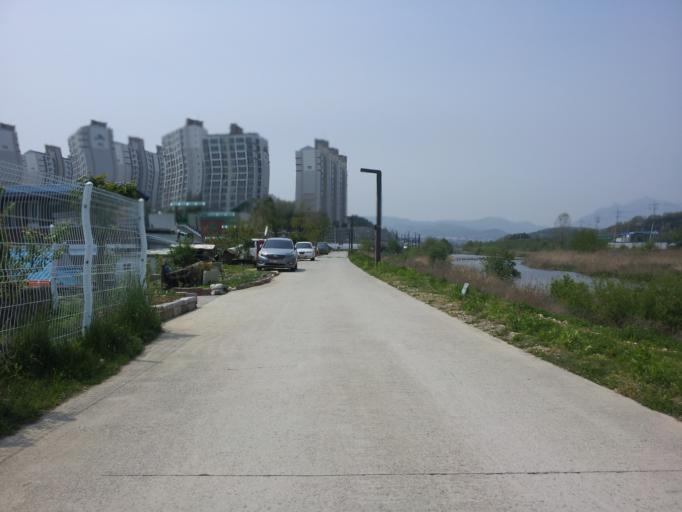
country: KR
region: Daejeon
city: Daejeon
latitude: 36.2674
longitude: 127.2761
